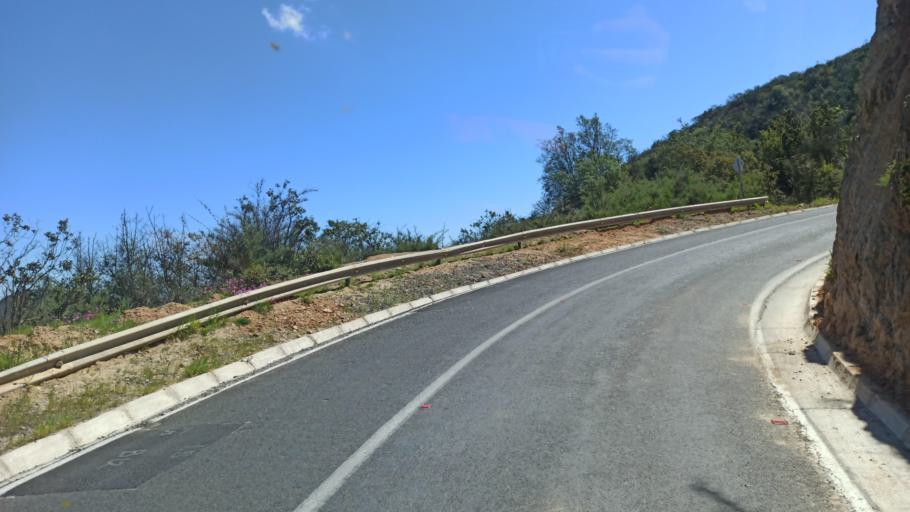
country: CL
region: Valparaiso
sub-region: Provincia de Marga Marga
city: Limache
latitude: -33.2055
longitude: -71.2540
